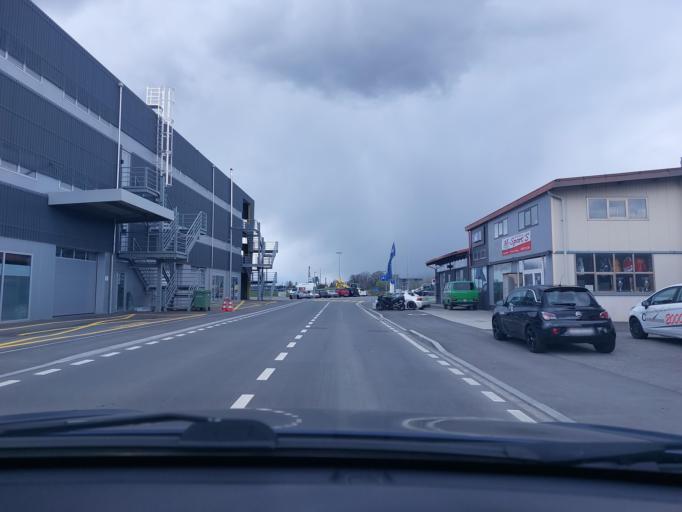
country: CH
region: Valais
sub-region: Monthey District
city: Collombey
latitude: 46.2687
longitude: 6.9589
